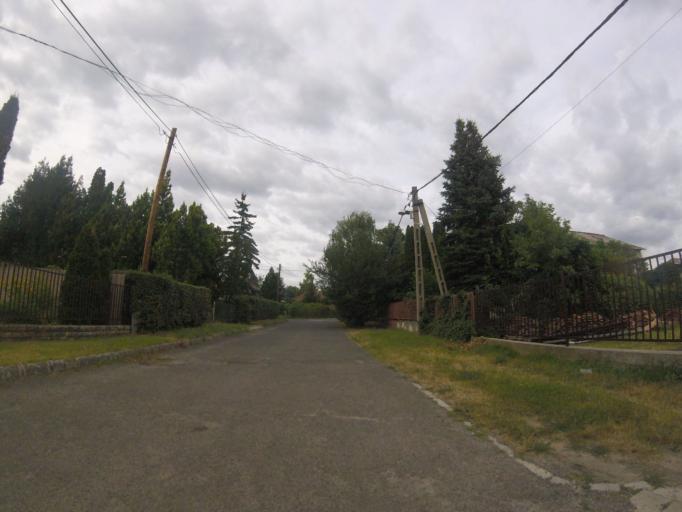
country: HU
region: Pest
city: Budakalasz
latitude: 47.5920
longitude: 19.0600
